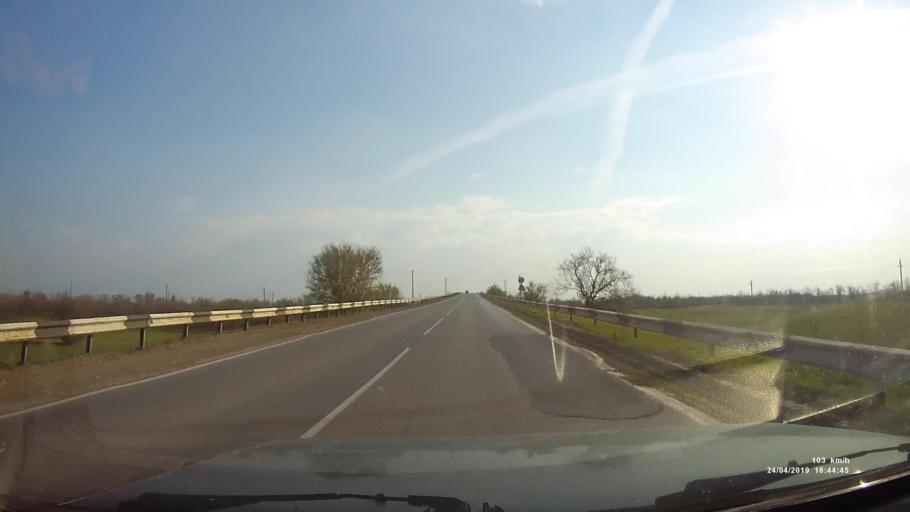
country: RU
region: Rostov
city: Gundorovskiy
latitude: 46.7777
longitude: 41.8232
